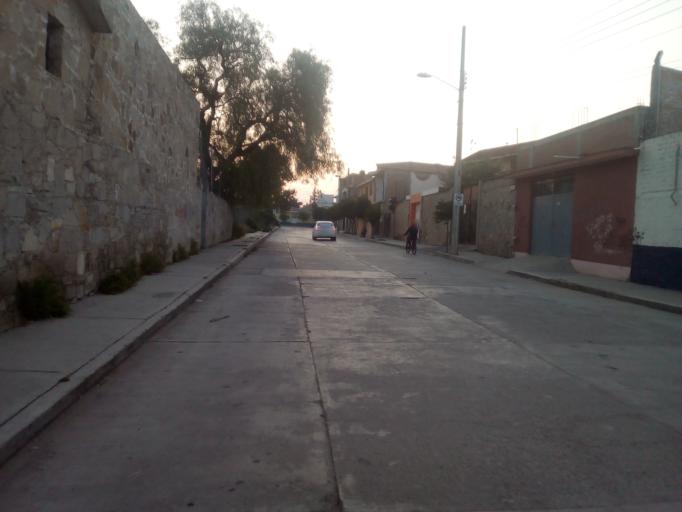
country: MX
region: Guerrero
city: San Luis de la Paz
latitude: 21.2907
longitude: -100.5263
